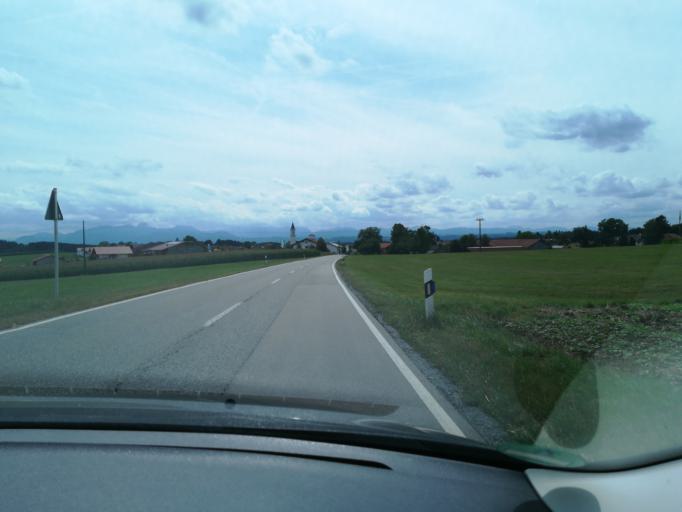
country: DE
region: Bavaria
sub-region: Upper Bavaria
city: Tuntenhausen
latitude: 47.9551
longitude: 11.9695
